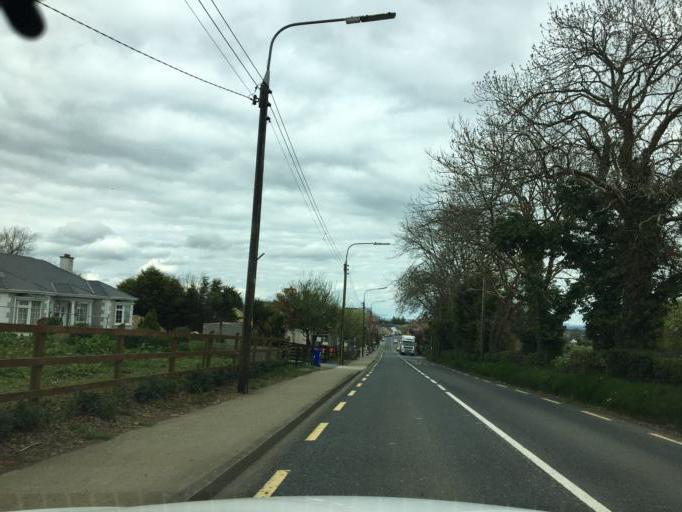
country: IE
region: Leinster
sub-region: Loch Garman
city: Enniscorthy
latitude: 52.4474
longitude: -6.7239
